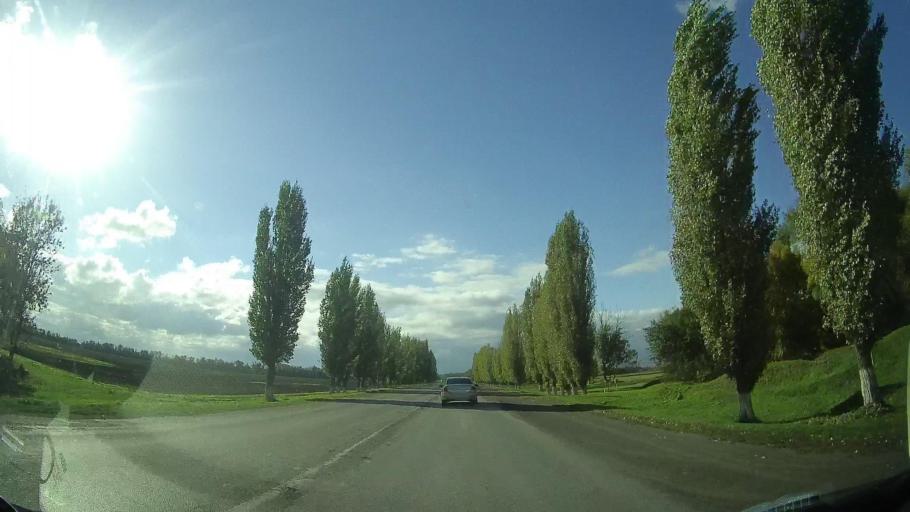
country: RU
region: Rostov
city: Tselina
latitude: 46.5323
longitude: 40.9997
